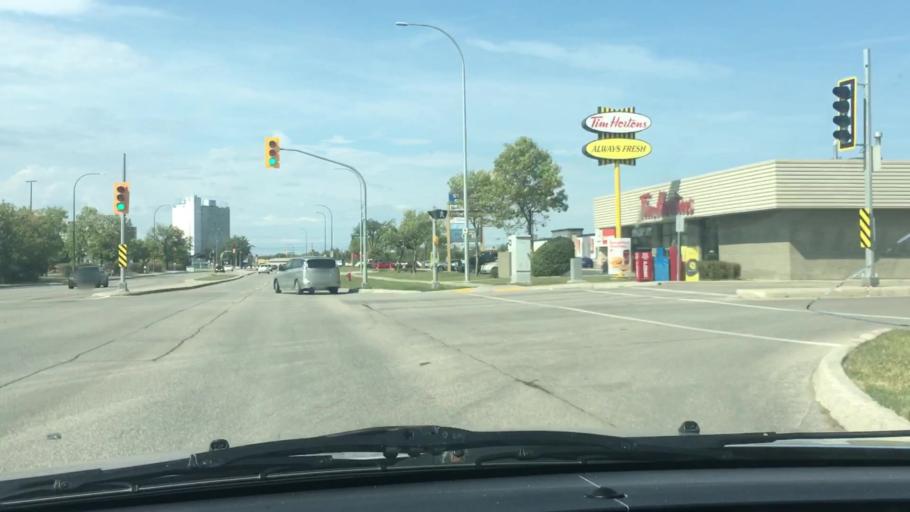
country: CA
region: Manitoba
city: Winnipeg
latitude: 49.8301
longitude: -97.1065
